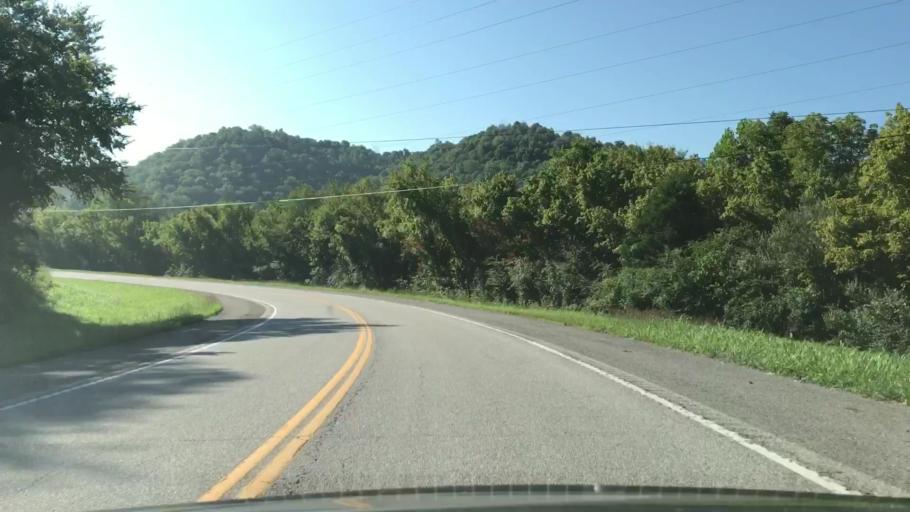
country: US
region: Tennessee
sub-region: Clay County
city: Celina
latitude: 36.4955
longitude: -85.5537
